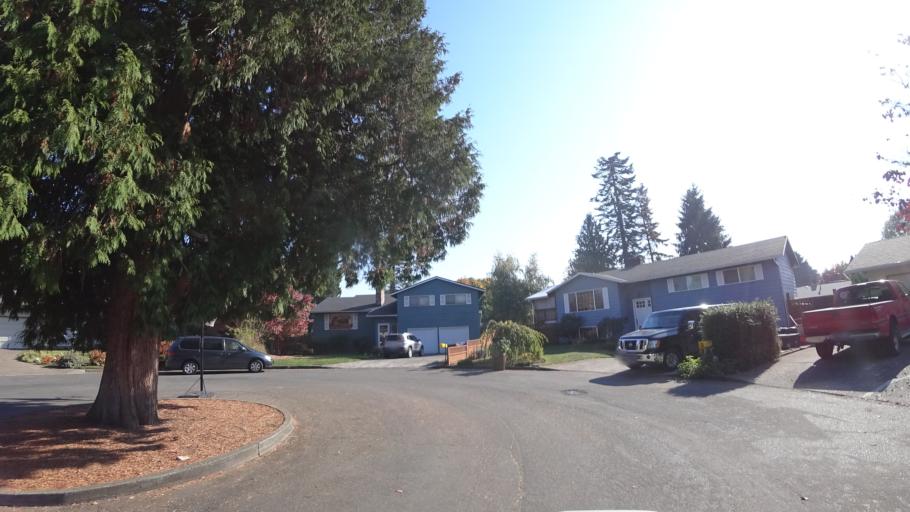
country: US
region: Oregon
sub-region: Multnomah County
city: Gresham
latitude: 45.5019
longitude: -122.4467
